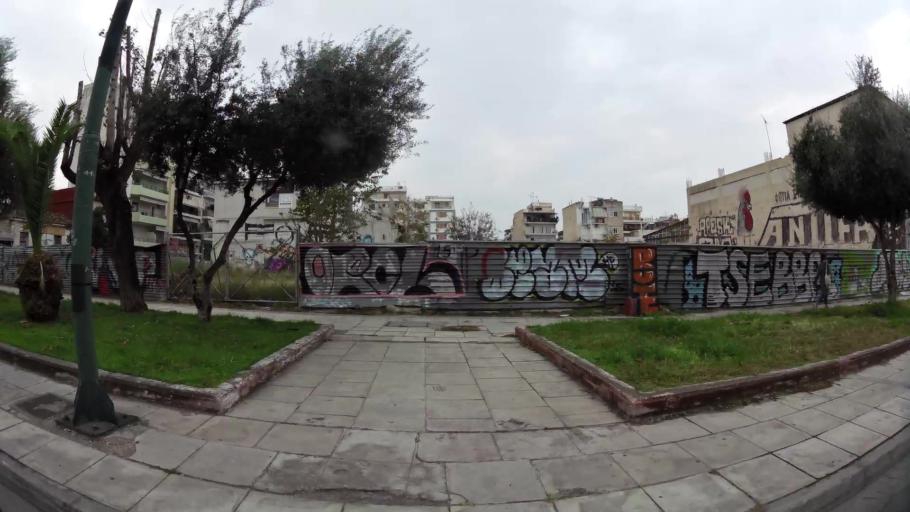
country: GR
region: Attica
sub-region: Nomarchia Athinas
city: Athens
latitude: 37.9813
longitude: 23.7105
